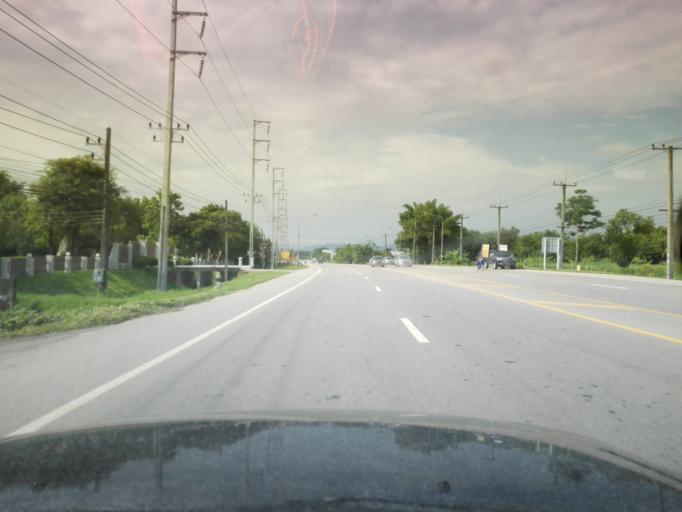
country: TH
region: Tak
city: Mae Sot
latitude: 16.7496
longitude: 98.5807
